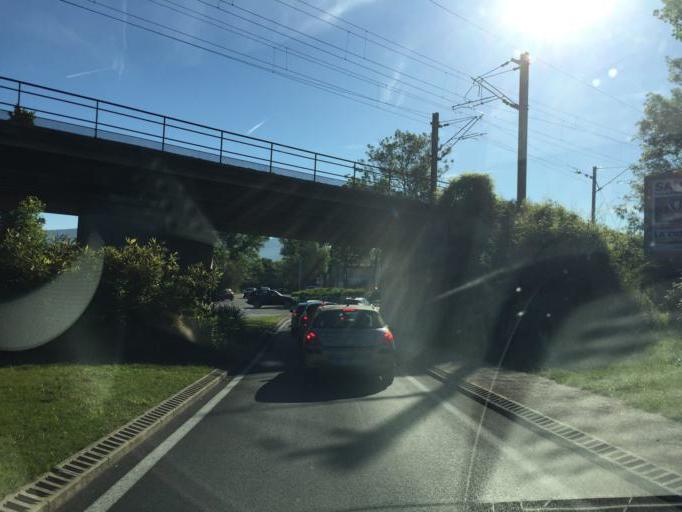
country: FR
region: Provence-Alpes-Cote d'Azur
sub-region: Departement des Bouches-du-Rhone
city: Aubagne
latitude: 43.2962
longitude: 5.5825
